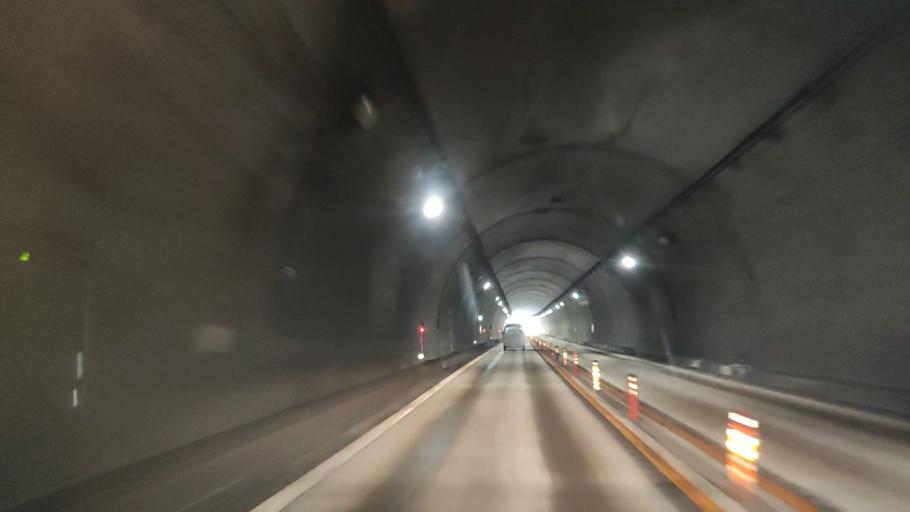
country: JP
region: Tokushima
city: Kamojimacho-jogejima
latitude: 34.1067
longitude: 134.2915
